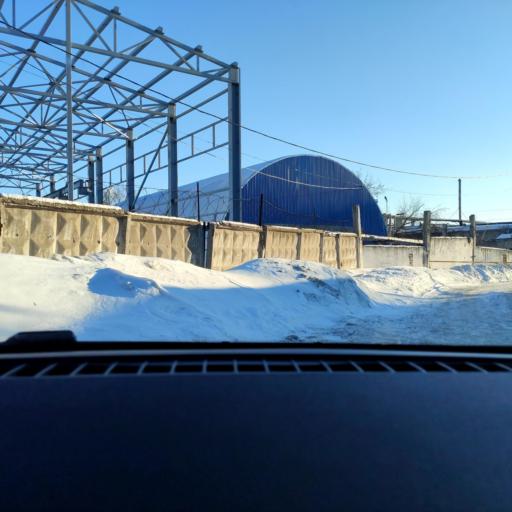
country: RU
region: Samara
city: Samara
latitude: 53.1312
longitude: 50.1044
